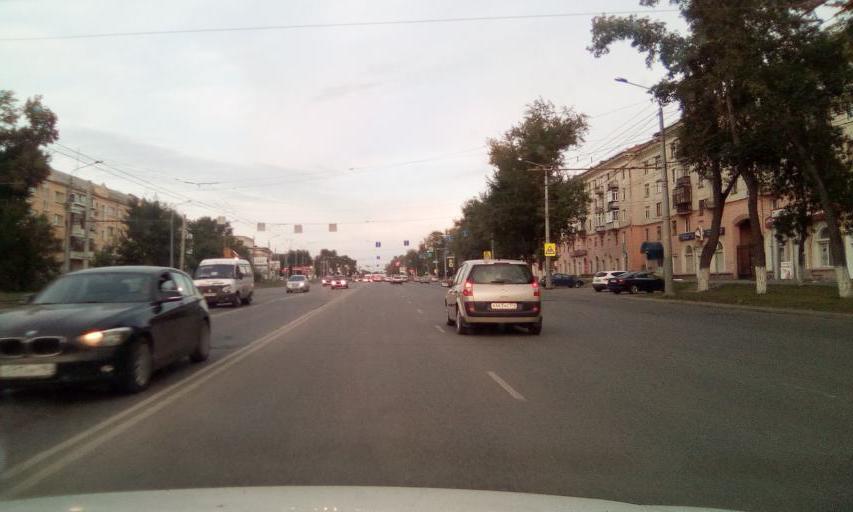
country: RU
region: Chelyabinsk
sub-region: Gorod Chelyabinsk
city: Chelyabinsk
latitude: 55.1605
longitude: 61.4463
